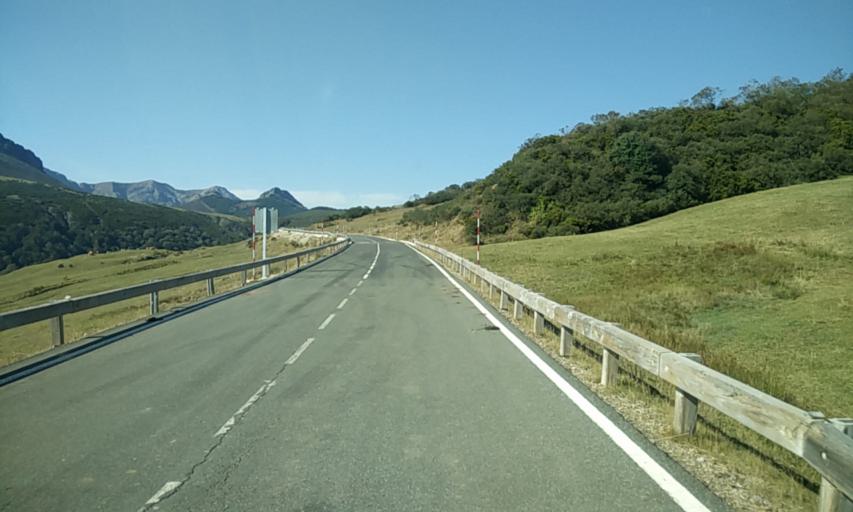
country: ES
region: Cantabria
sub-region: Provincia de Cantabria
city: Camaleno
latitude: 43.0714
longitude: -4.7502
